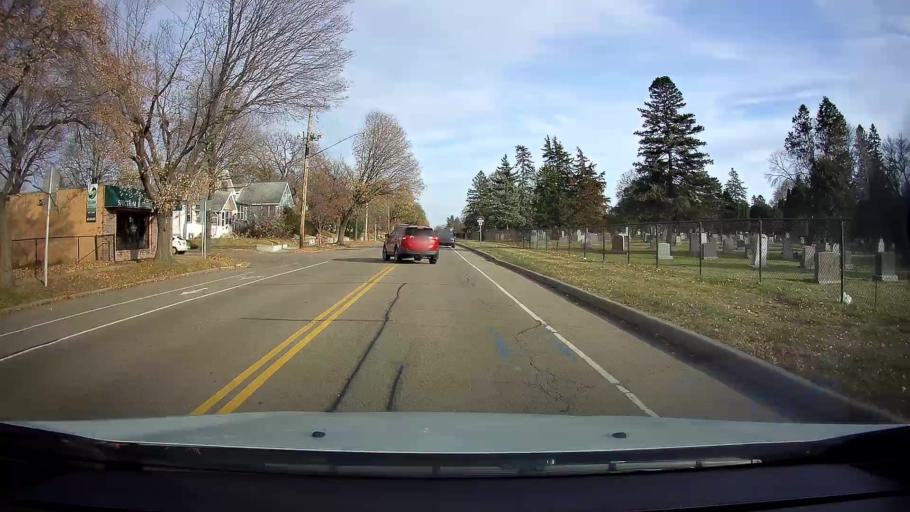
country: US
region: Minnesota
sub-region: Ramsey County
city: Falcon Heights
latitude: 44.9702
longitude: -93.1408
